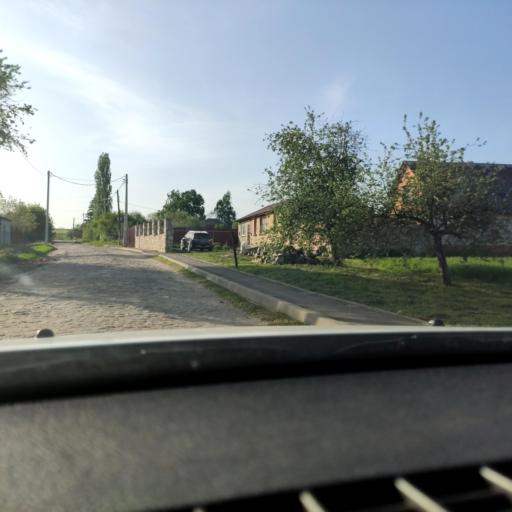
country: RU
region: Voronezj
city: Devitsa
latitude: 51.6416
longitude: 38.9548
